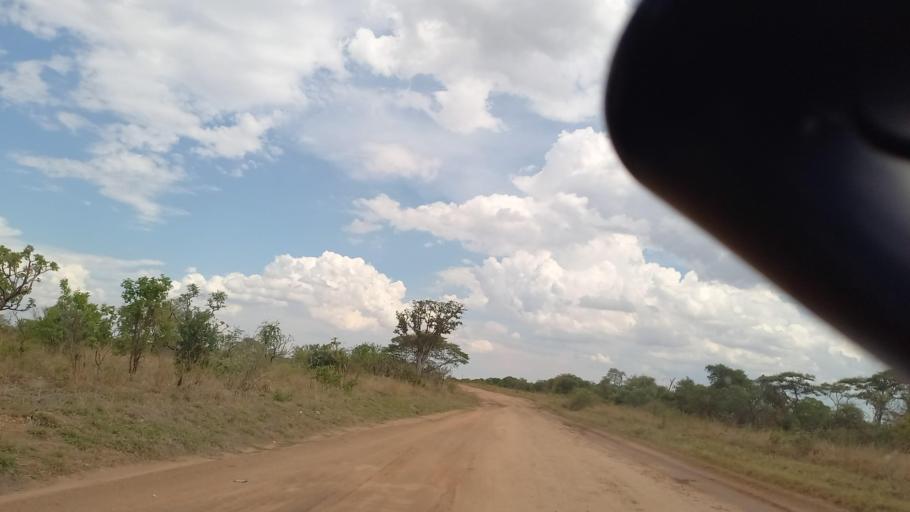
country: ZM
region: Southern
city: Nakambala
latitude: -16.0570
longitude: 27.9887
